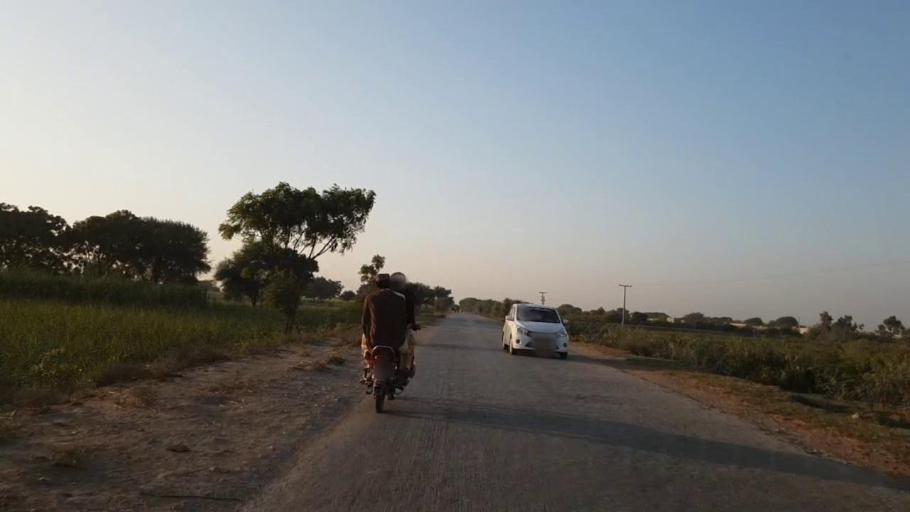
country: PK
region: Sindh
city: Chambar
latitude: 25.2365
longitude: 68.6977
